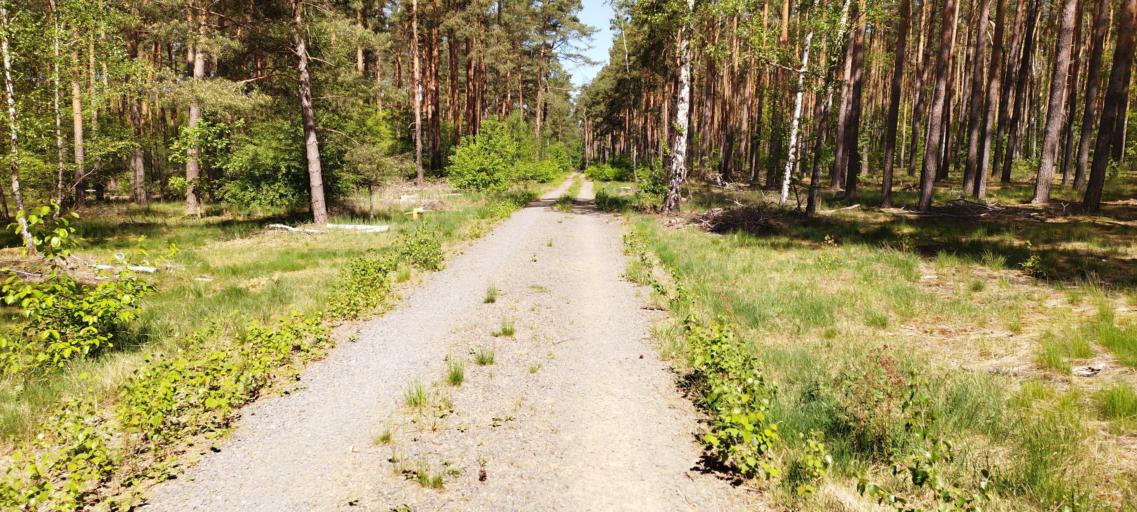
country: DE
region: Berlin
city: Muggelheim
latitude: 52.4026
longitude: 13.6956
